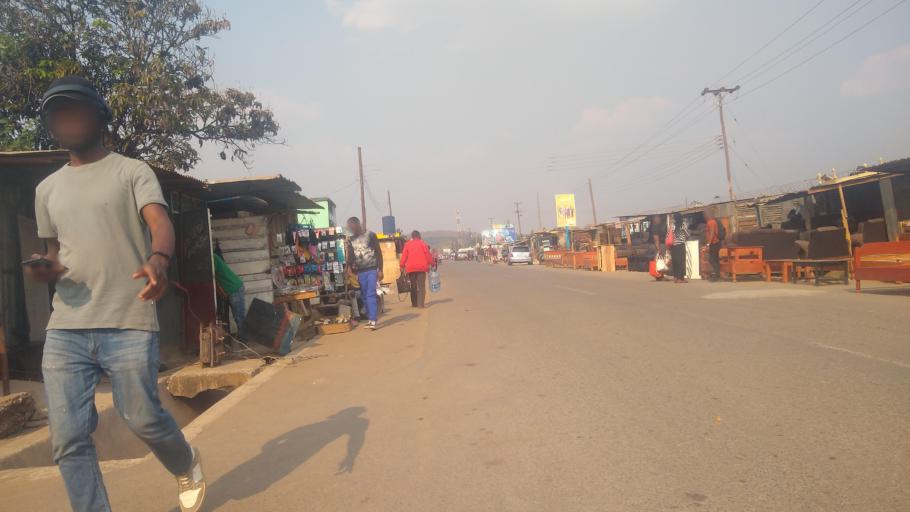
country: ZM
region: Lusaka
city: Lusaka
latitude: -15.4477
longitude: 28.3764
